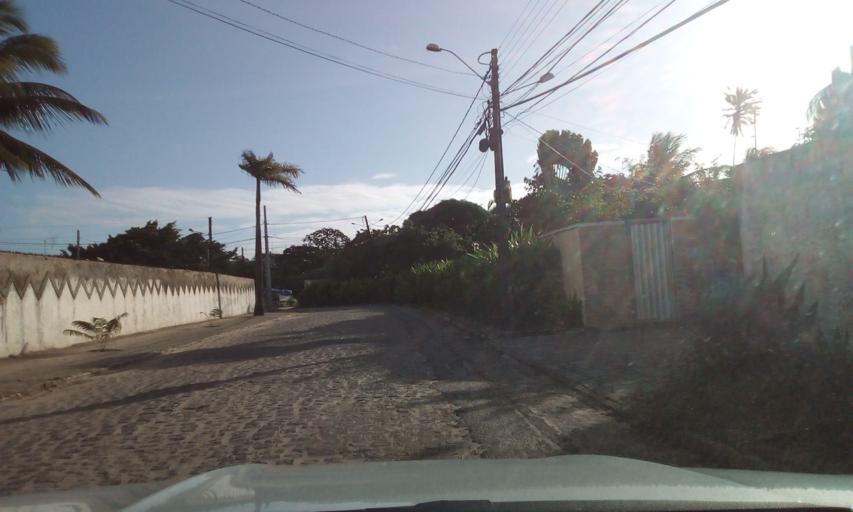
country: BR
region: Paraiba
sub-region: Joao Pessoa
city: Joao Pessoa
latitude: -7.1631
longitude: -34.8529
